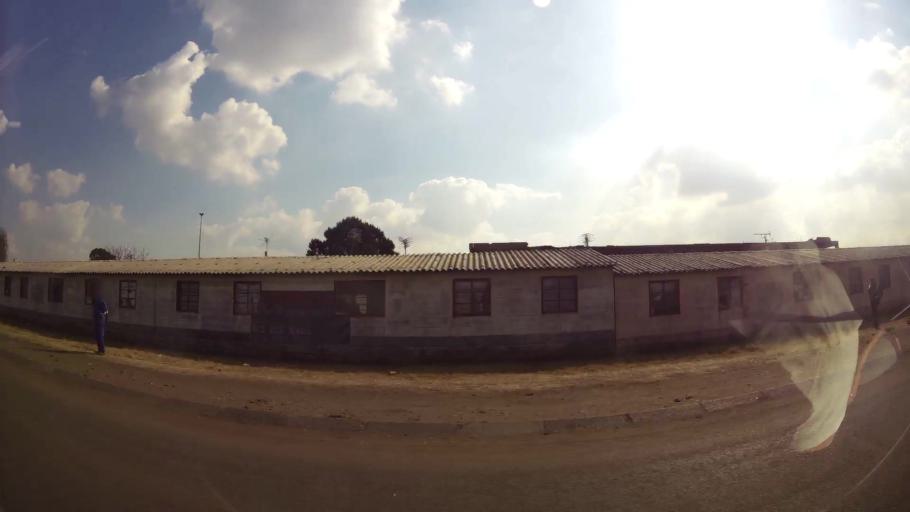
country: ZA
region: Gauteng
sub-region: Ekurhuleni Metropolitan Municipality
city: Germiston
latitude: -26.3382
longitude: 28.1402
